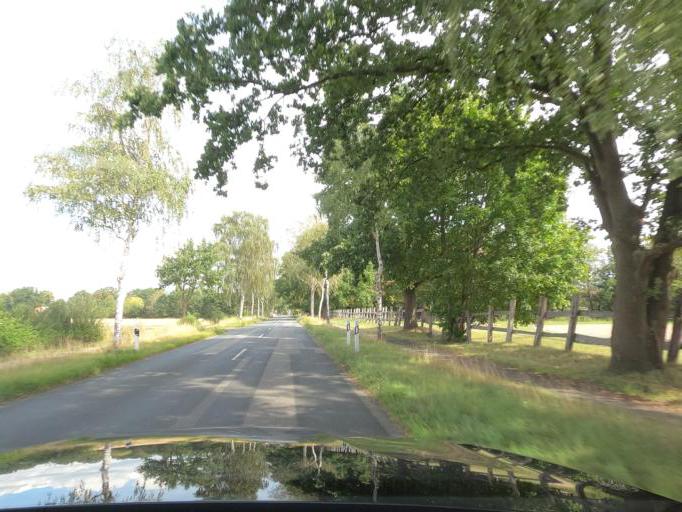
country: DE
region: Lower Saxony
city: Burgdorf
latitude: 52.4661
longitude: 9.9683
